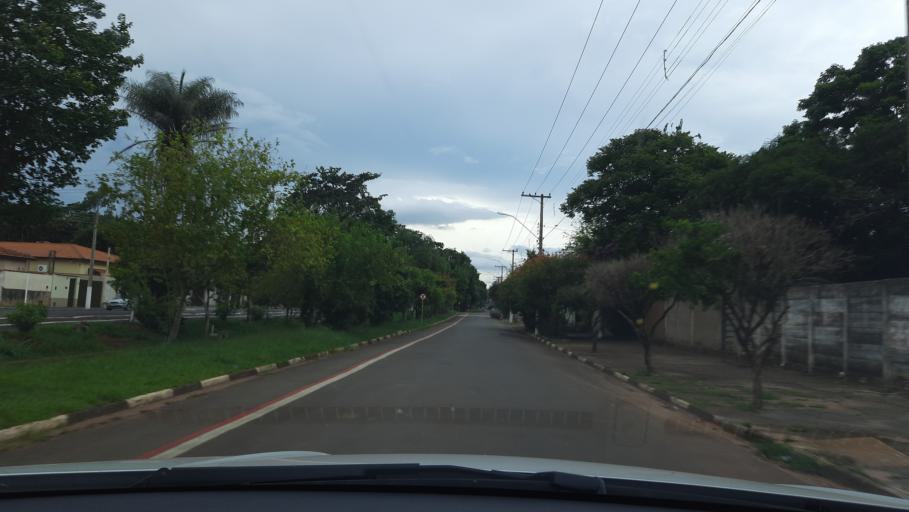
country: BR
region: Sao Paulo
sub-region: Casa Branca
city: Casa Branca
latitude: -21.7683
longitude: -47.0877
